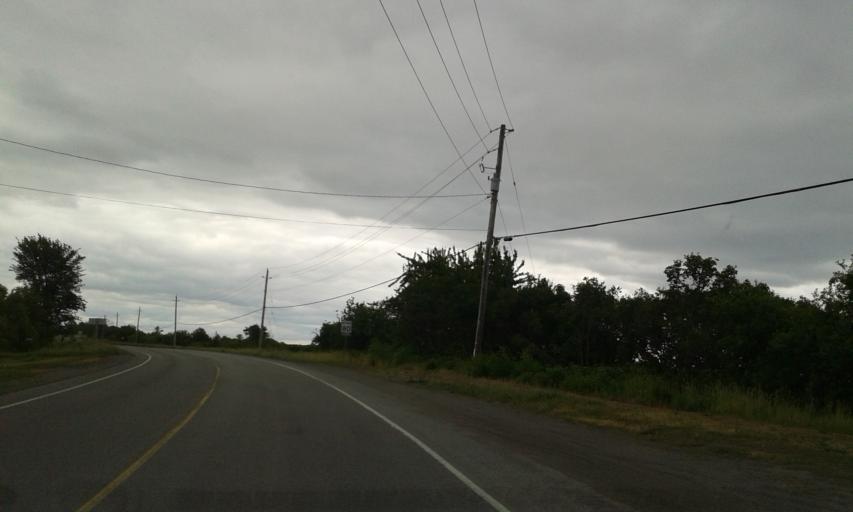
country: CA
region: Ontario
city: Prince Edward
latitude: 43.9721
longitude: -77.4521
